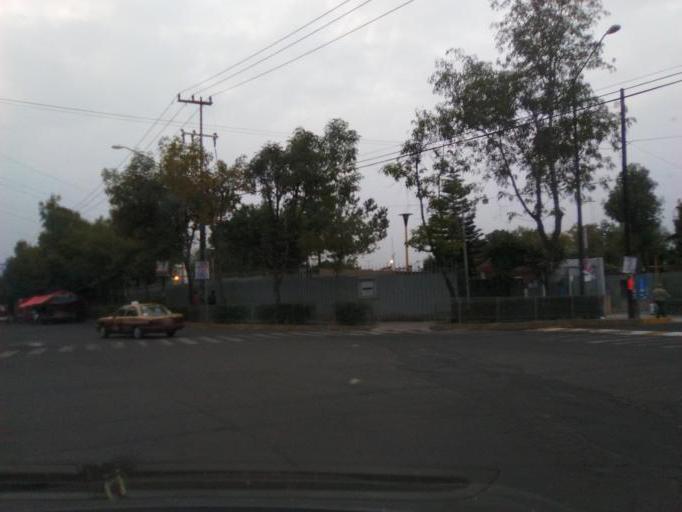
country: MX
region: Mexico City
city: Magdalena Contreras
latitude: 19.3062
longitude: -99.2185
